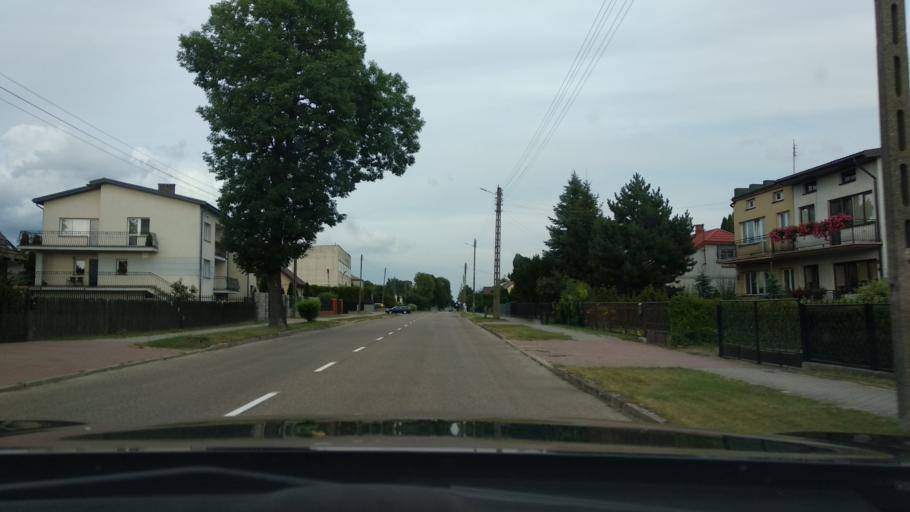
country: PL
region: Masovian Voivodeship
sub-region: Powiat pultuski
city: Obryte
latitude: 52.7160
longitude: 21.2445
